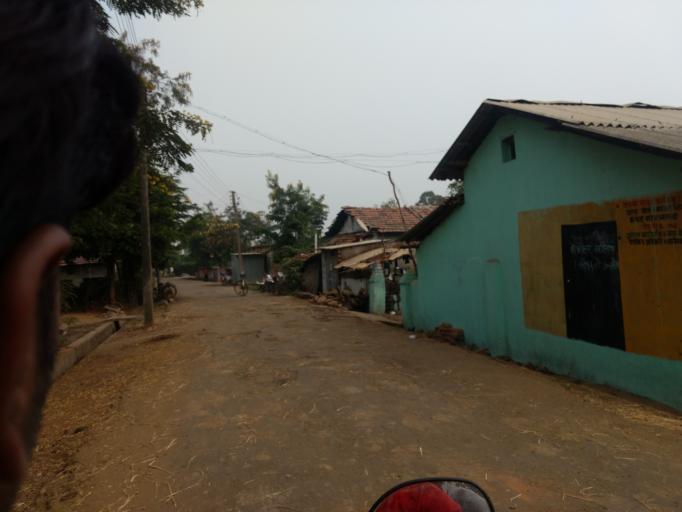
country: IN
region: Maharashtra
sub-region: Chandrapur
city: Mul
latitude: 19.9184
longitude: 79.9475
